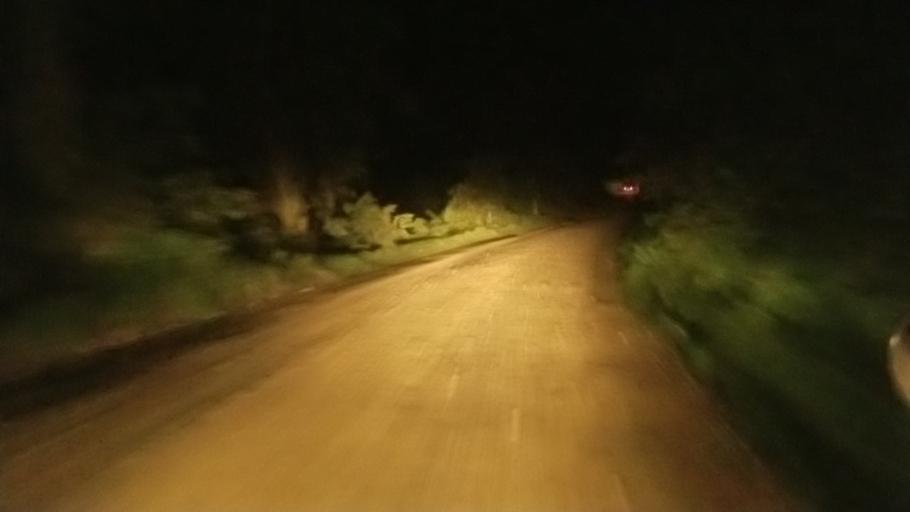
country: RW
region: Western Province
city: Cyangugu
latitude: -2.1358
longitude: 28.8601
